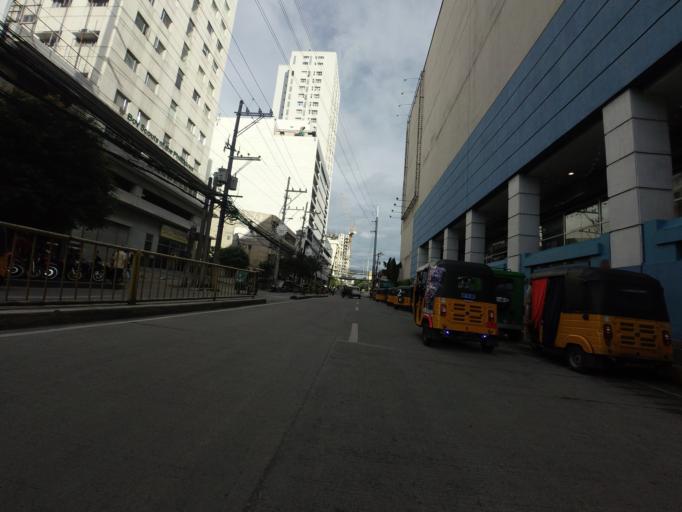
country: PH
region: Metro Manila
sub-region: City of Manila
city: Quiapo
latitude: 14.5903
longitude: 120.9832
